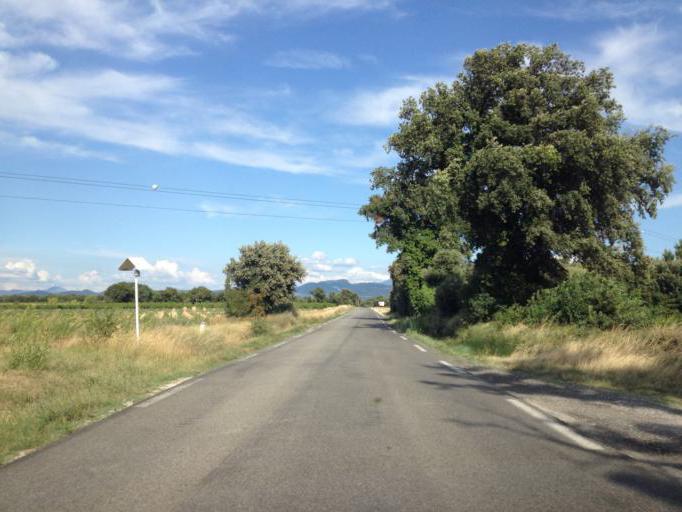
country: FR
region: Provence-Alpes-Cote d'Azur
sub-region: Departement du Vaucluse
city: Camaret-sur-Aigues
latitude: 44.1643
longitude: 4.8980
